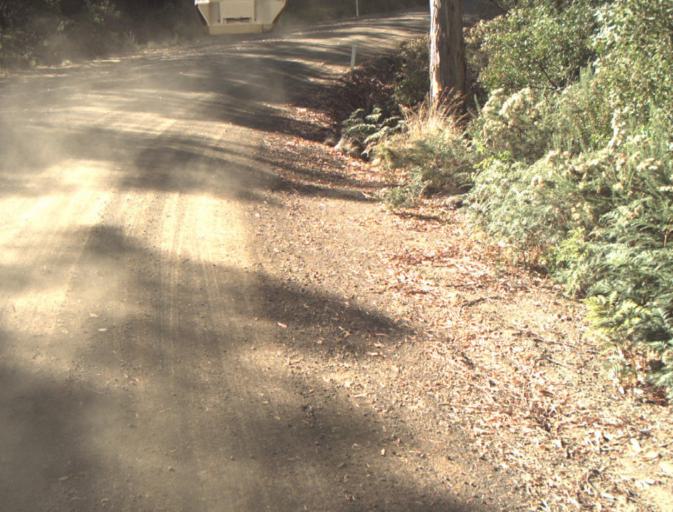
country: AU
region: Tasmania
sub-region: Launceston
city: Newstead
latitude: -41.3086
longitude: 147.3355
